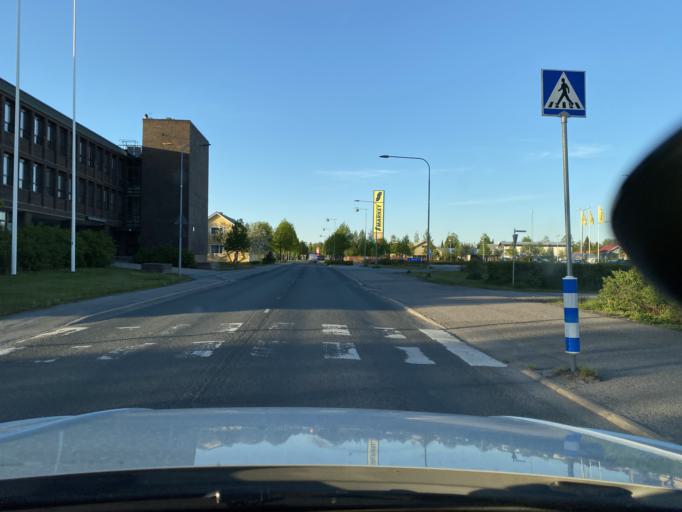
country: FI
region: Satakunta
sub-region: Pori
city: Huittinen
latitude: 61.1767
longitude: 22.7000
